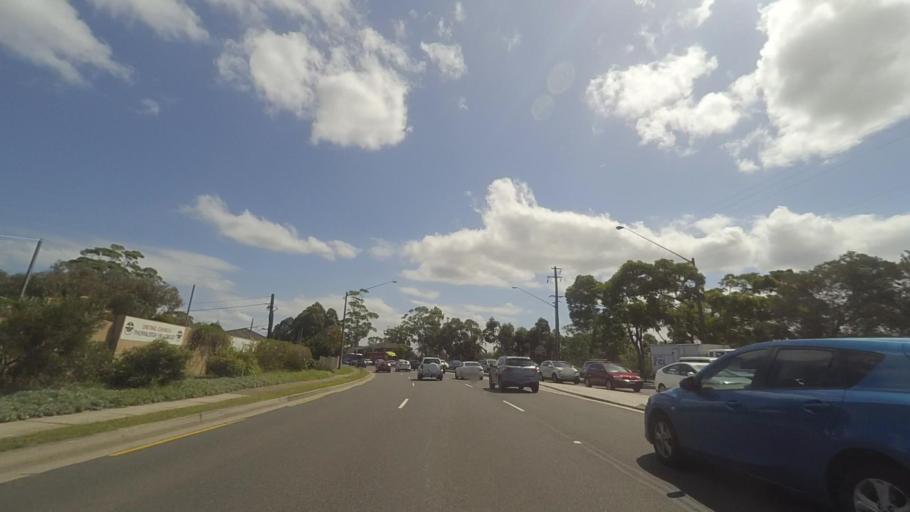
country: AU
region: New South Wales
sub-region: Hornsby Shire
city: Pennant Hills
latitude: -33.7329
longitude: 151.0780
